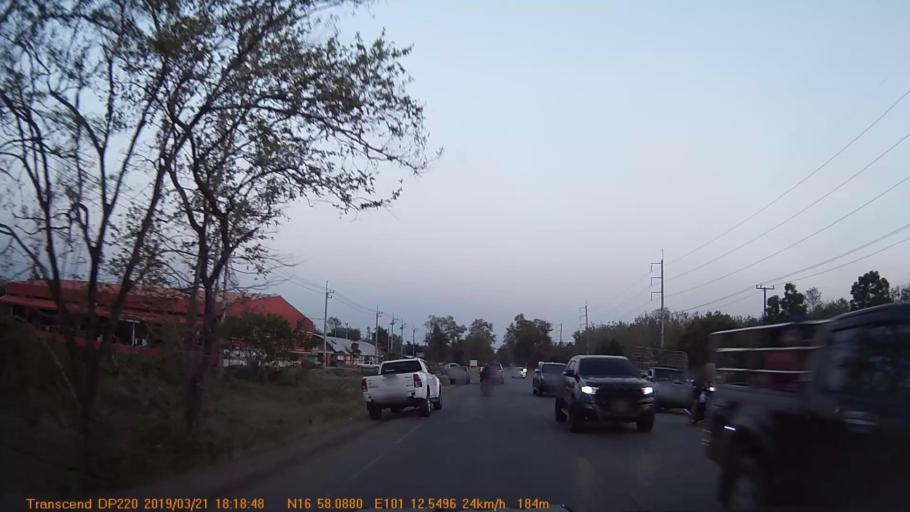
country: TH
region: Phetchabun
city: Lom Kao
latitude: 16.9680
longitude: 101.2092
